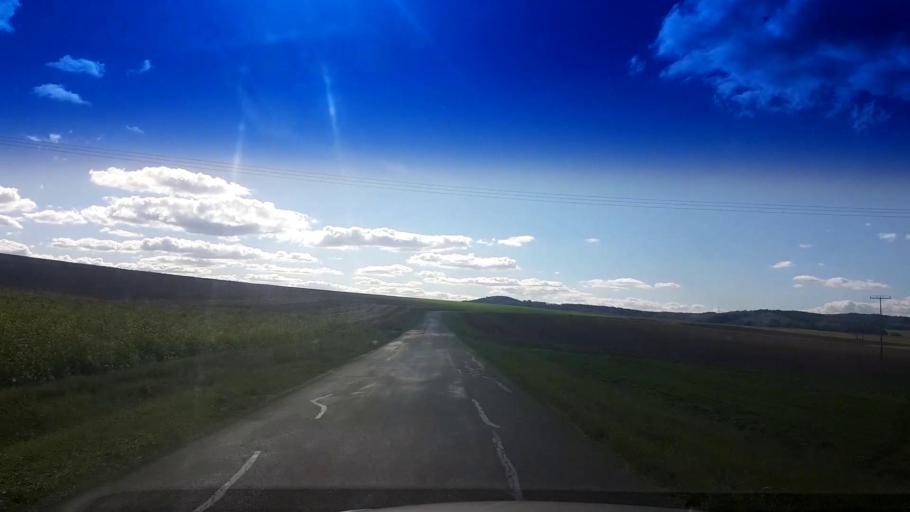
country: DE
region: Bavaria
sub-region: Upper Franconia
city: Arzberg
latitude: 50.0256
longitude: 12.2324
